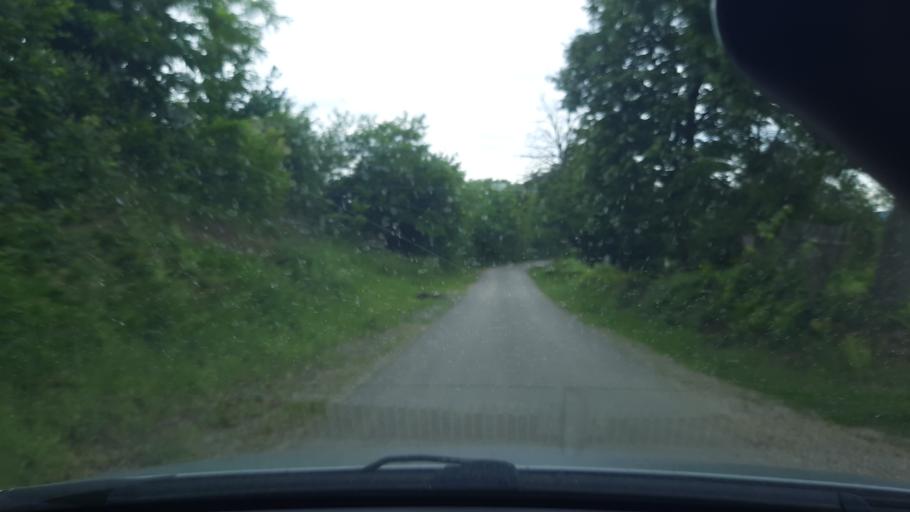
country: RS
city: Jarebice
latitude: 44.5073
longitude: 19.4759
